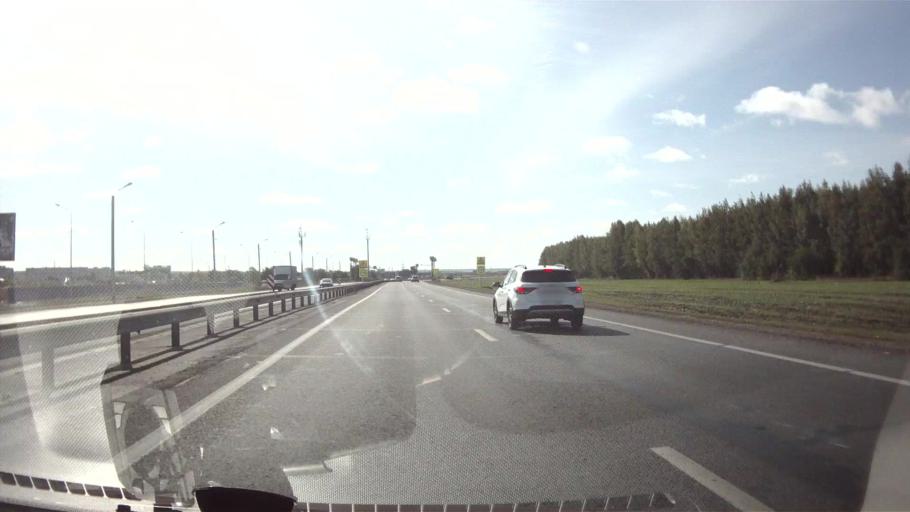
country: RU
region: Ulyanovsk
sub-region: Ulyanovskiy Rayon
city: Ulyanovsk
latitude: 54.2782
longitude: 48.2593
